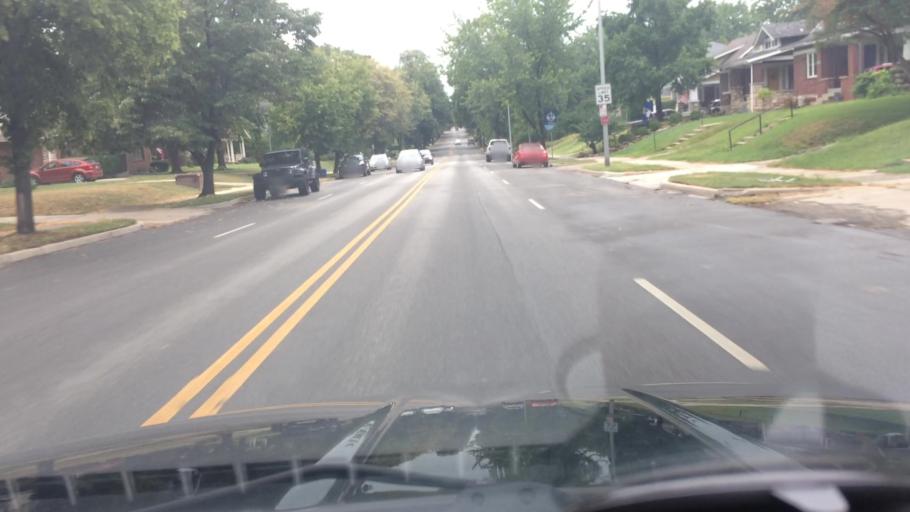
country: US
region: Kansas
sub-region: Johnson County
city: Mission Hills
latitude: 39.0241
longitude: -94.5762
